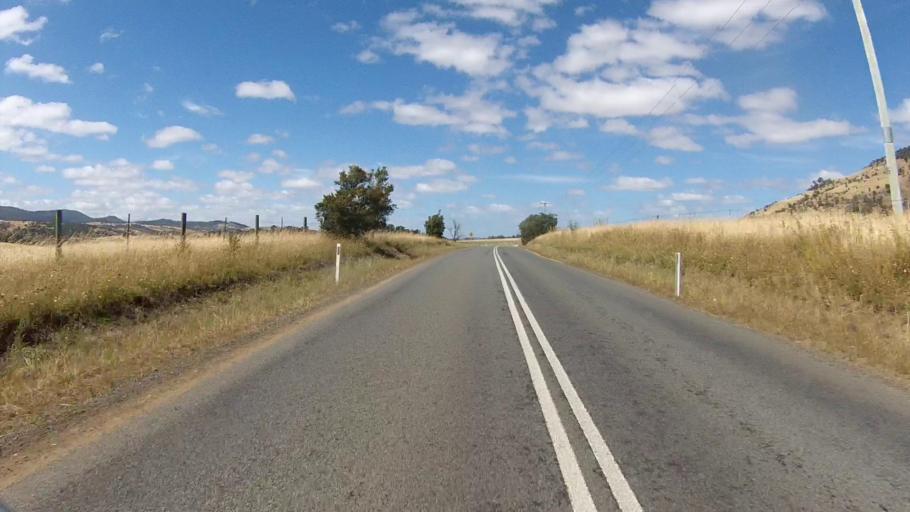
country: AU
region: Tasmania
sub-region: Sorell
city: Sorell
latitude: -42.6312
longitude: 147.4294
